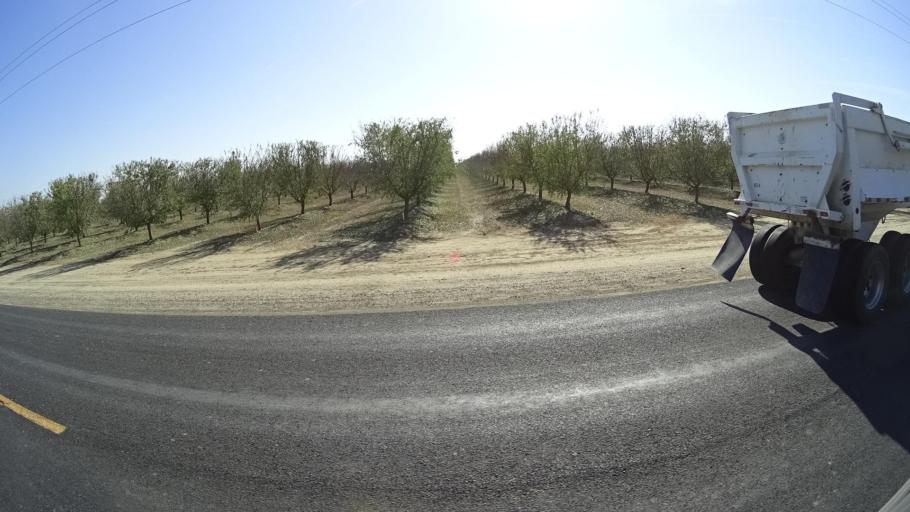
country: US
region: California
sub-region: Kern County
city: McFarland
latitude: 35.6455
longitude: -119.2441
